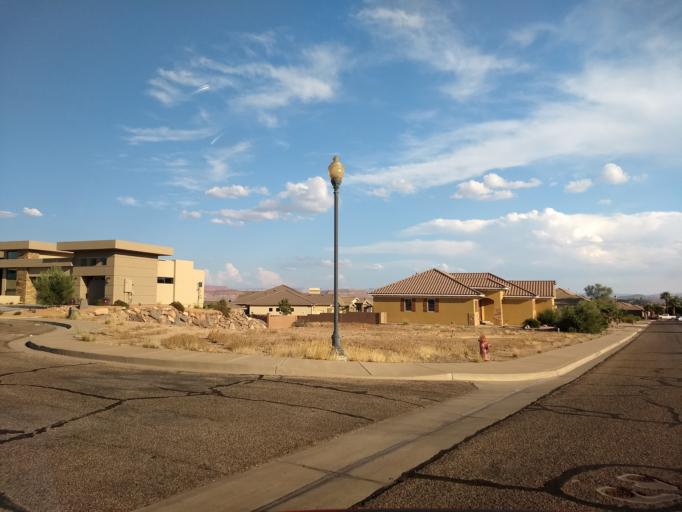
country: US
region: Utah
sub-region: Washington County
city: Saint George
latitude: 37.0976
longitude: -113.5458
